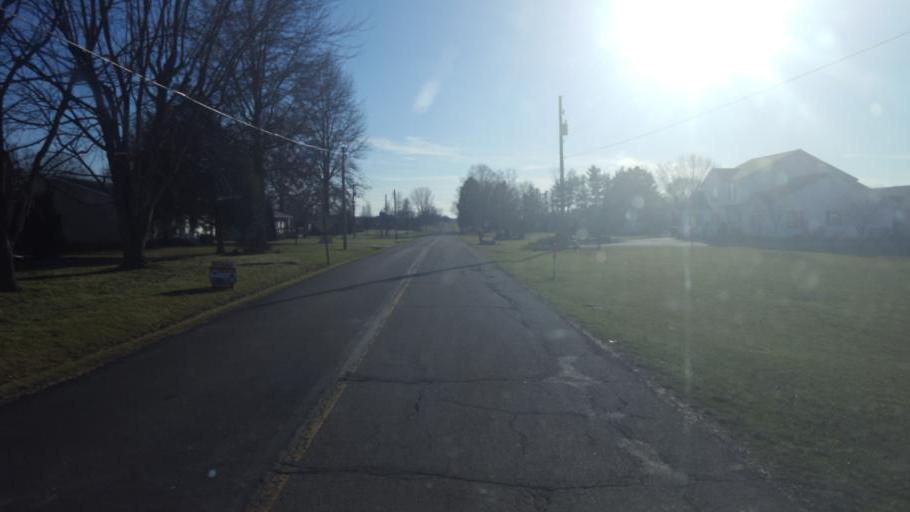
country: US
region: Ohio
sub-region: Knox County
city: Fredericktown
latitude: 40.4723
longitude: -82.5495
